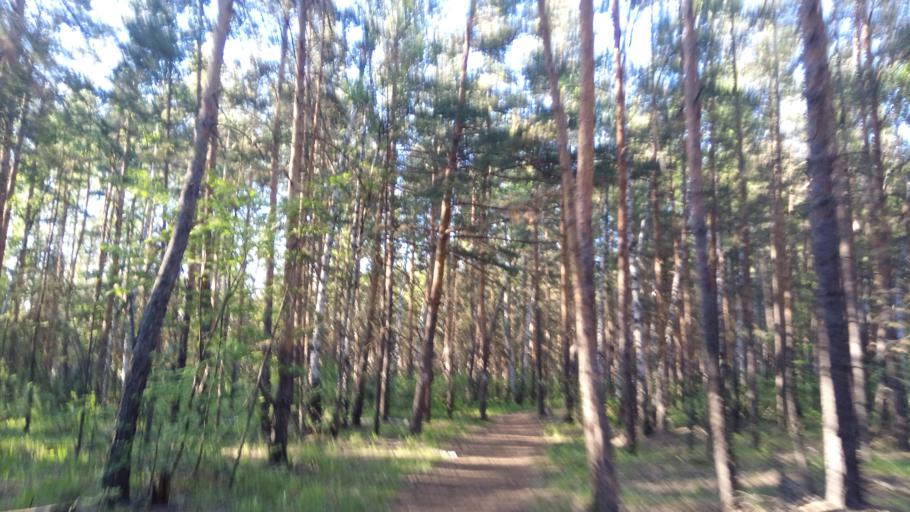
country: RU
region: Chelyabinsk
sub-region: Gorod Chelyabinsk
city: Chelyabinsk
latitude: 55.1297
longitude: 61.3393
